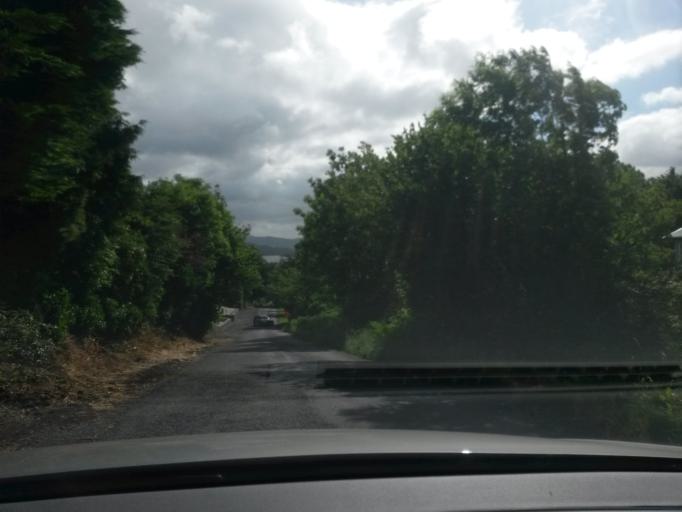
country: IE
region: Connaught
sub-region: Sligo
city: Sligo
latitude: 54.2510
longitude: -8.4466
